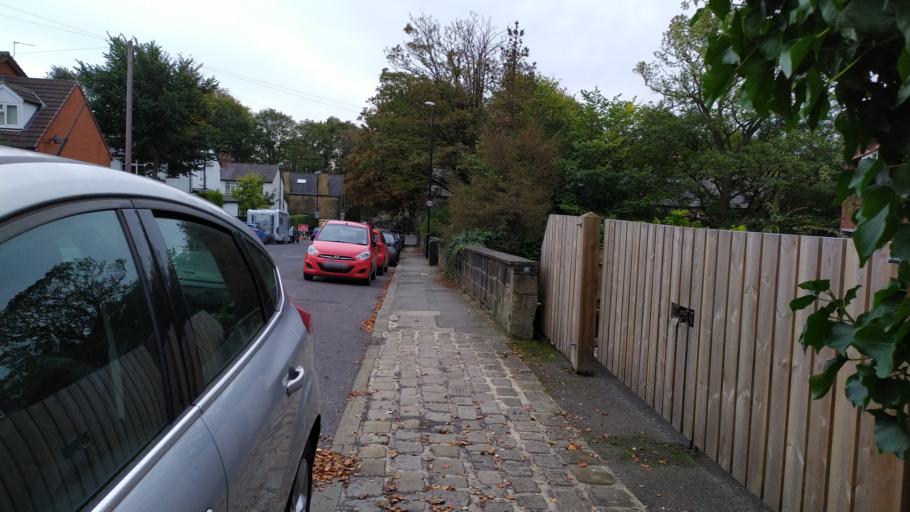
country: GB
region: England
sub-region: City and Borough of Leeds
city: Chapel Allerton
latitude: 53.8266
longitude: -1.5760
